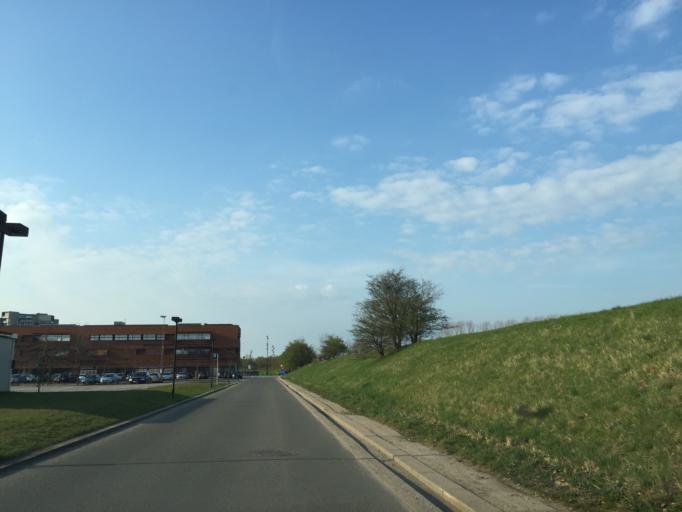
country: DK
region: South Denmark
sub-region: Odense Kommune
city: Neder Holluf
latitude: 55.3689
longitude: 10.4325
